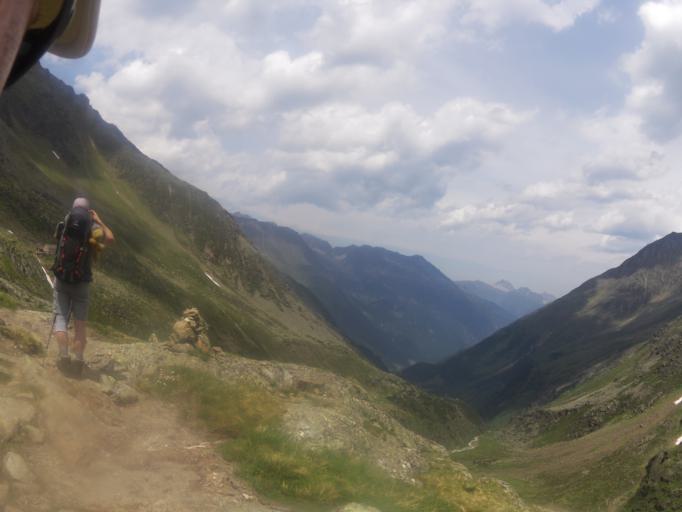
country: IT
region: Trentino-Alto Adige
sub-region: Bolzano
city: Racines
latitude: 46.9903
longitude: 11.2223
